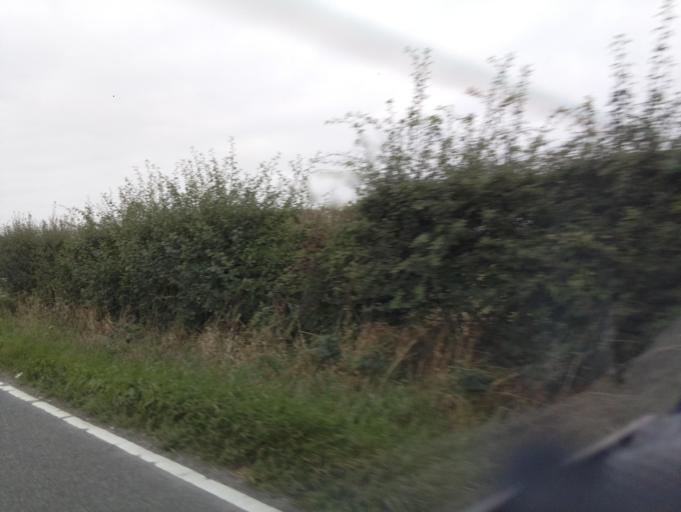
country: GB
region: England
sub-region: Shropshire
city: Astley
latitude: 52.7568
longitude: -2.6957
